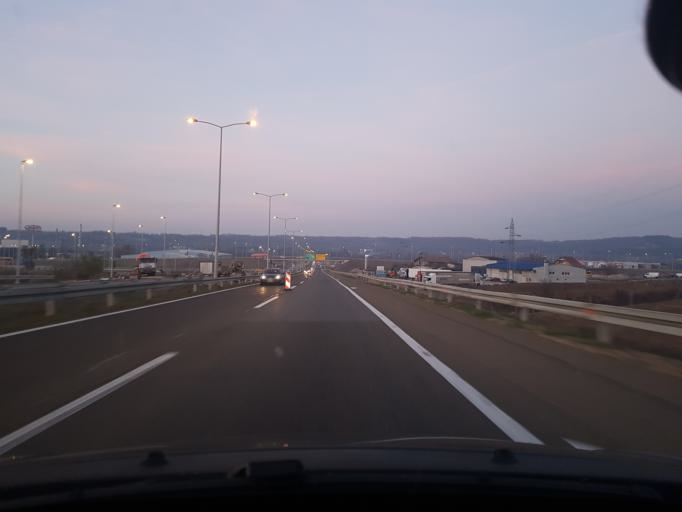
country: RS
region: Central Serbia
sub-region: Pomoravski Okrug
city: Paracin
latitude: 43.8535
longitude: 21.4348
